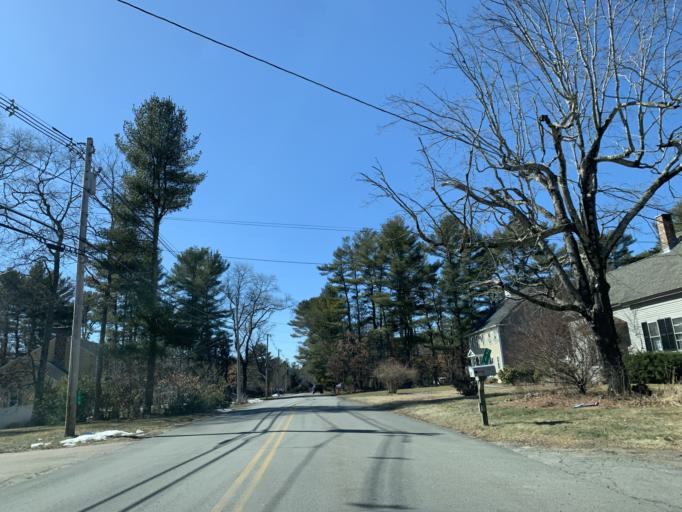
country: US
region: Massachusetts
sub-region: Bristol County
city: Norton
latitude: 41.9465
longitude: -71.1711
